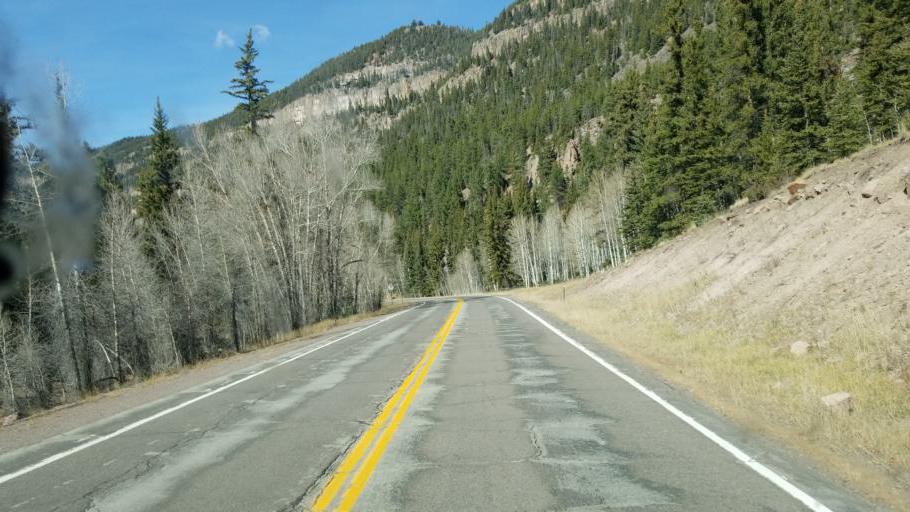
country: US
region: Colorado
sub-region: Conejos County
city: Conejos
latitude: 37.1145
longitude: -106.3219
